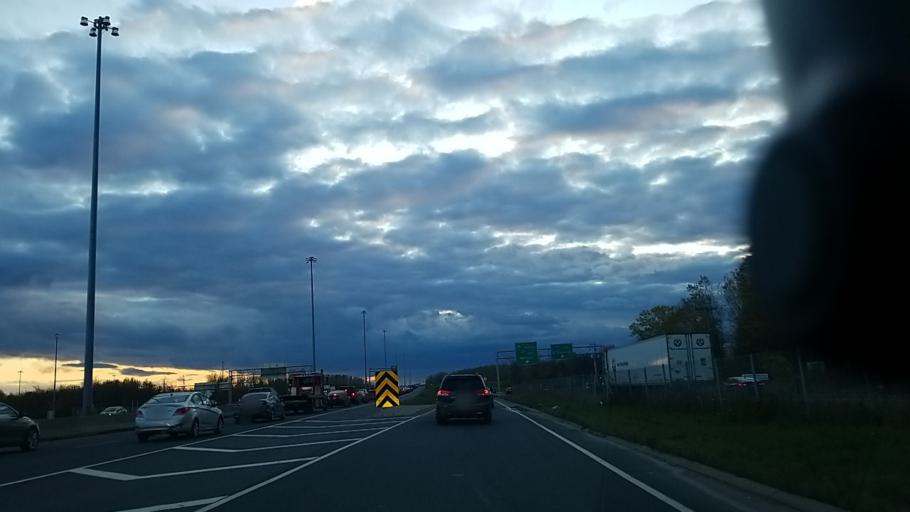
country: CA
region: Quebec
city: Dollard-Des Ormeaux
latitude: 45.5565
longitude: -73.8034
